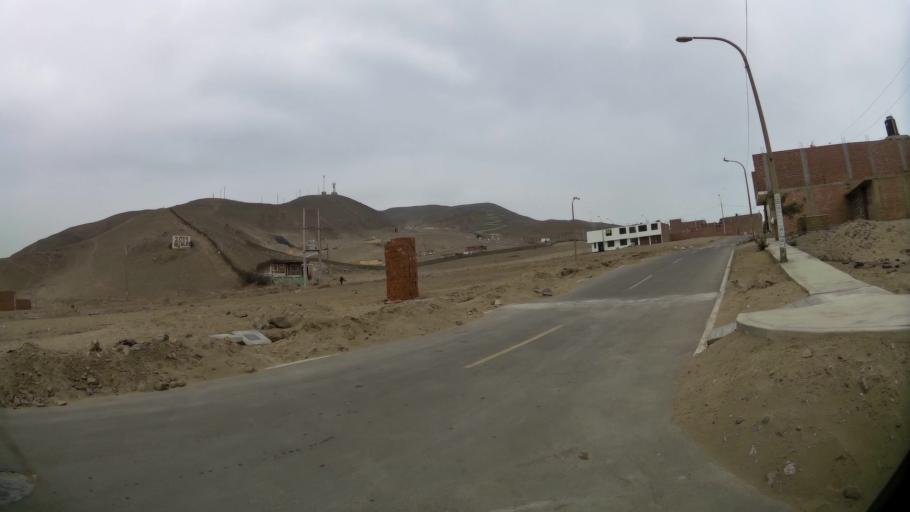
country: PE
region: Lima
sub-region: Lima
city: Santa Rosa
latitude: -11.7907
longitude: -77.1557
